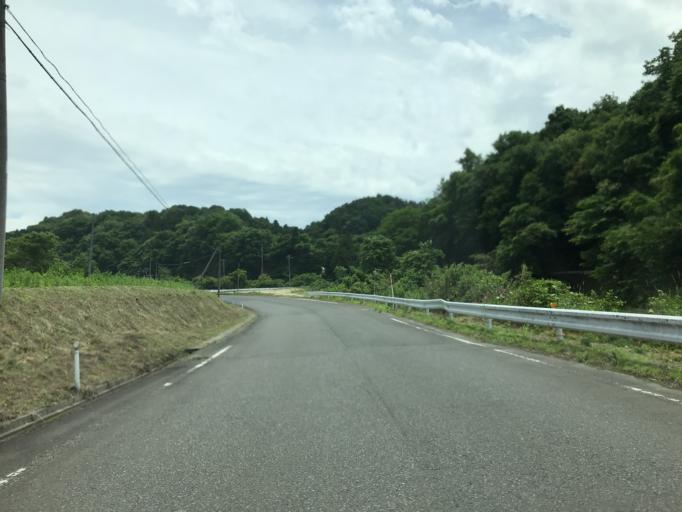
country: JP
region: Fukushima
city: Miharu
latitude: 37.4187
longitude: 140.5156
